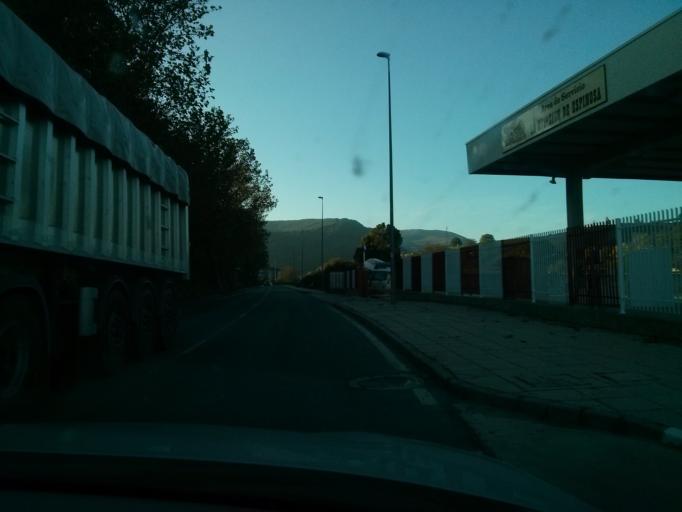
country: ES
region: Castille and Leon
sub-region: Provincia de Burgos
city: Espinosa de los Monteros
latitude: 43.0752
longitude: -3.5425
